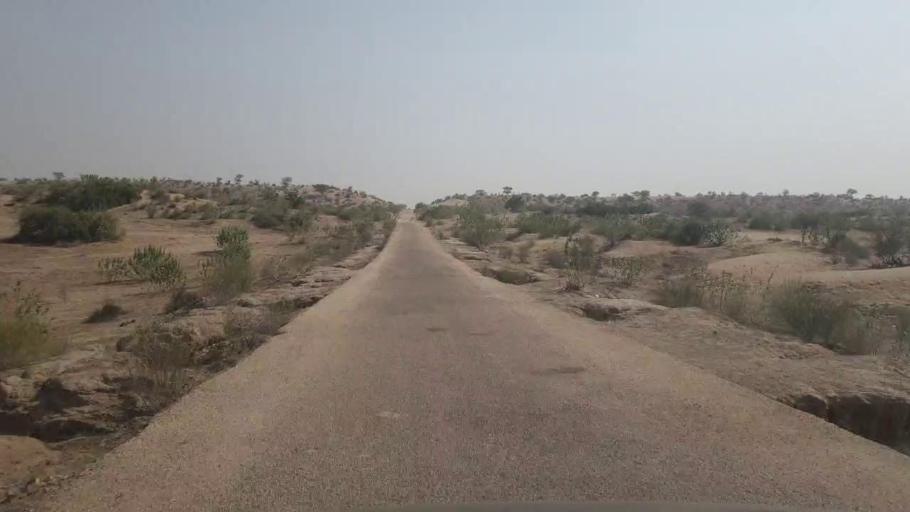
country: PK
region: Sindh
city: Chor
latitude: 25.5933
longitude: 70.0040
